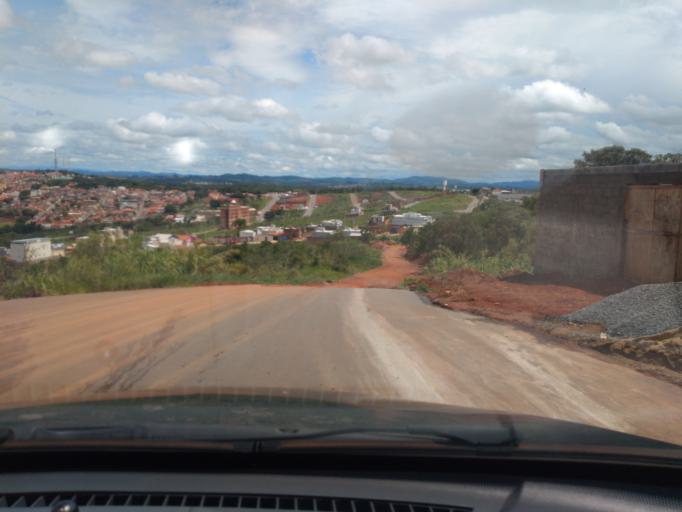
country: BR
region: Minas Gerais
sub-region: Tres Coracoes
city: Tres Coracoes
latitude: -21.6749
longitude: -45.2780
